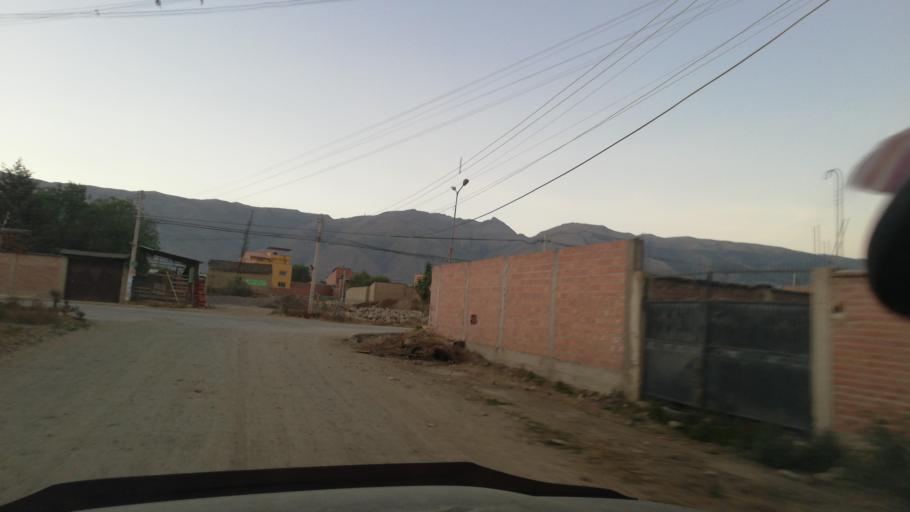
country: BO
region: Cochabamba
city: Cochabamba
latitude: -17.3841
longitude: -66.2188
